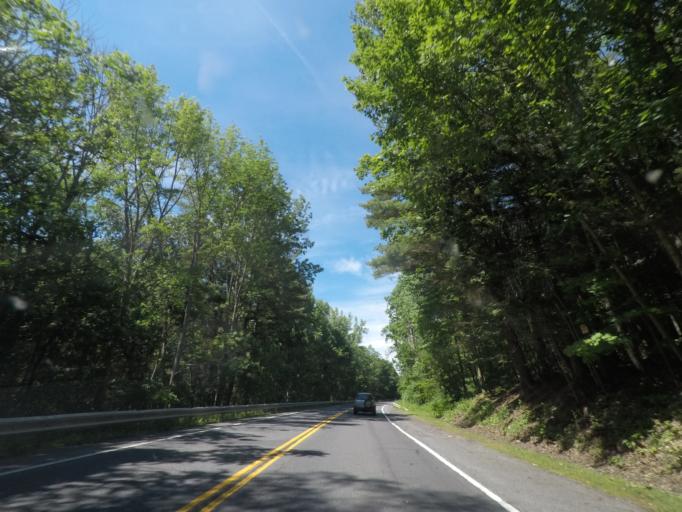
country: US
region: Massachusetts
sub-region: Berkshire County
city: Richmond
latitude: 42.4009
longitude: -73.4084
